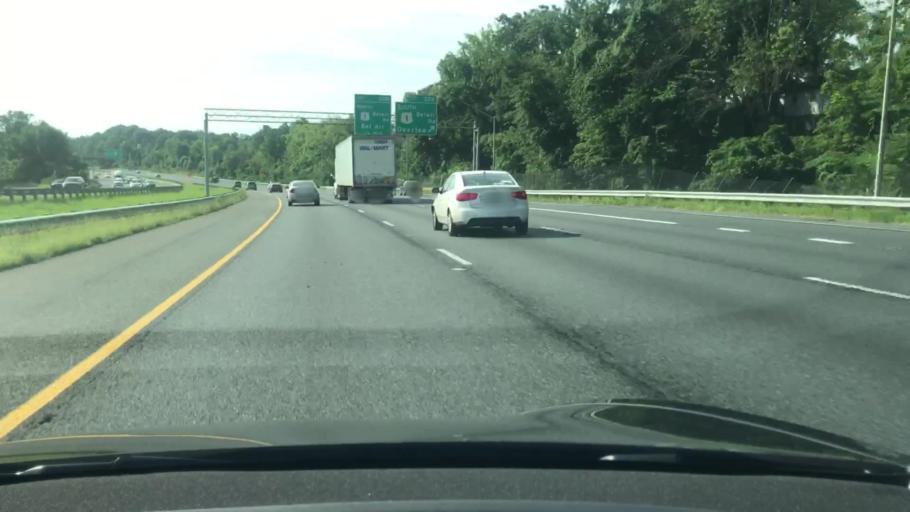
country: US
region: Maryland
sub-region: Baltimore County
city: Overlea
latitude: 39.3741
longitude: -76.5171
